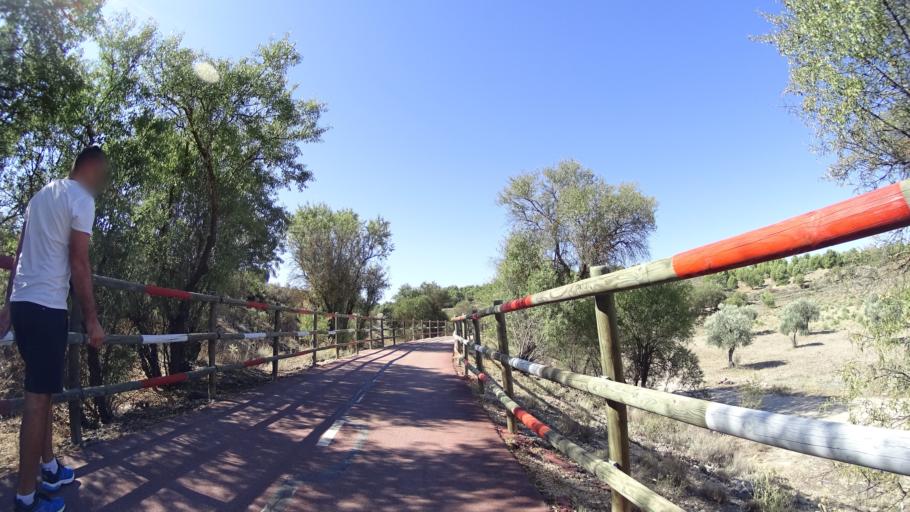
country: ES
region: Madrid
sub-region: Provincia de Madrid
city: Arganda
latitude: 40.2729
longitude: -3.4497
